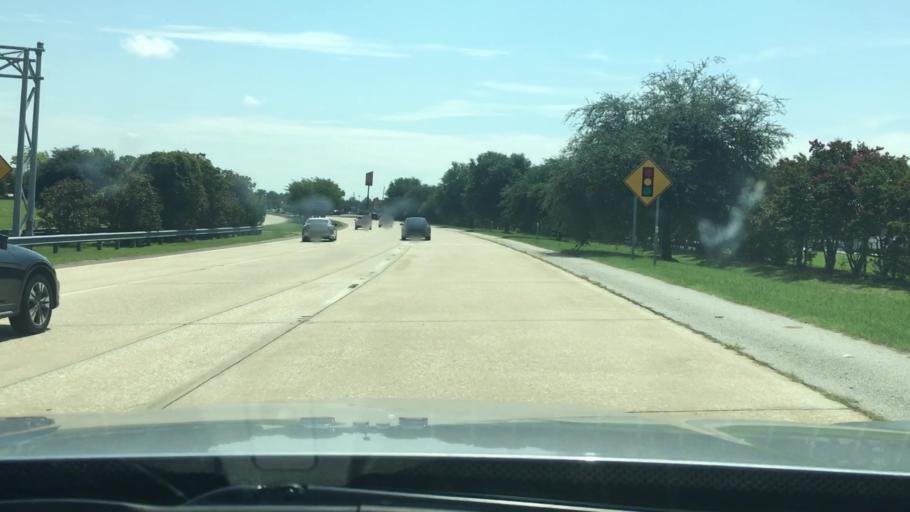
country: US
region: South Carolina
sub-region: Florence County
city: Florence
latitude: 34.1906
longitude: -79.8402
